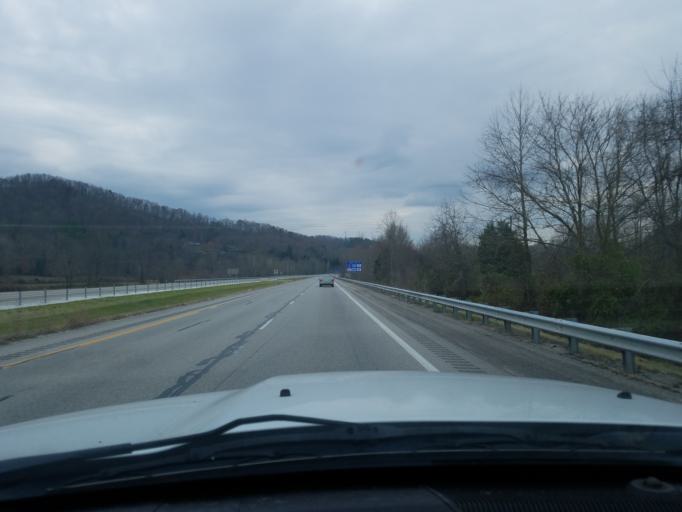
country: US
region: Kentucky
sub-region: Rowan County
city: Morehead
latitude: 38.2018
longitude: -83.4672
